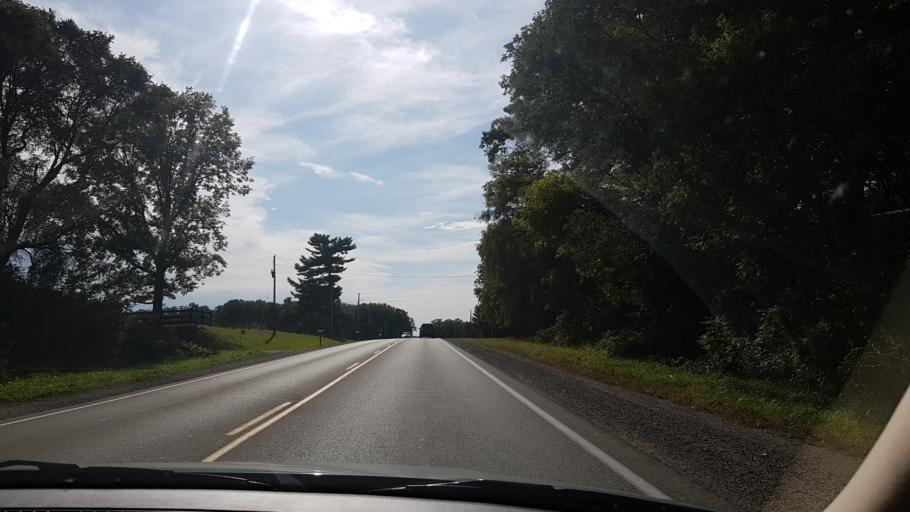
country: CA
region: Ontario
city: Delaware
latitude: 42.9377
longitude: -81.4412
